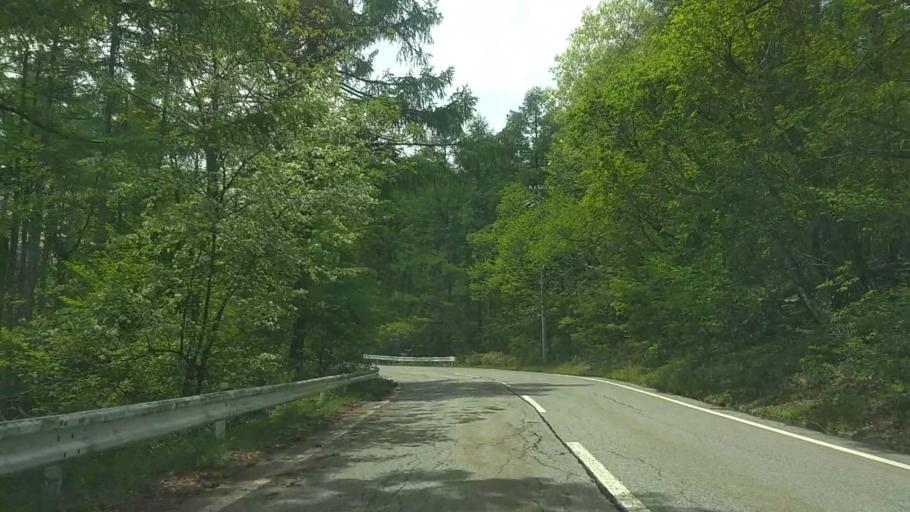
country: JP
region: Nagano
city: Saku
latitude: 36.1054
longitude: 138.3984
